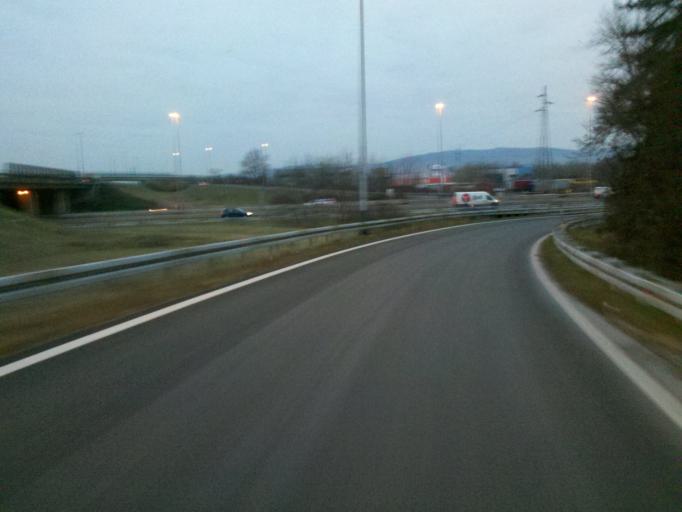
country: HR
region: Grad Zagreb
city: Zadvorsko
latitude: 45.7582
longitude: 15.9008
